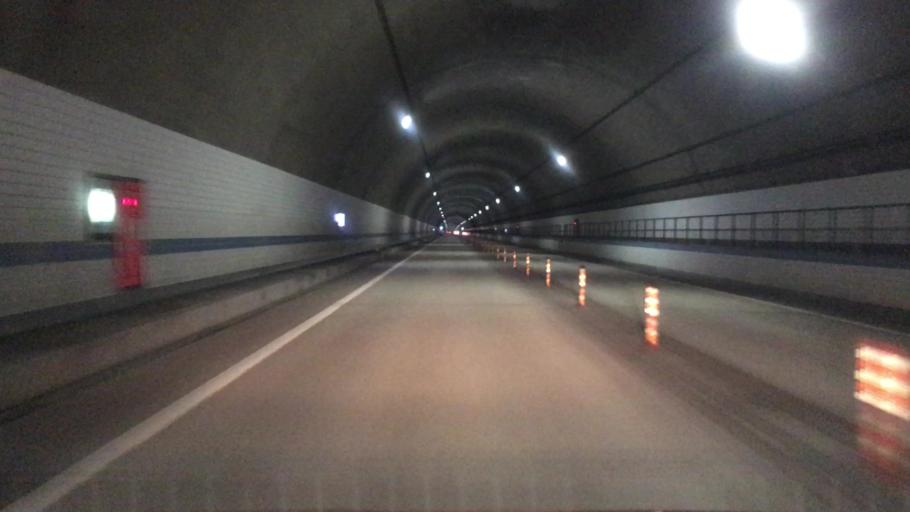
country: JP
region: Hyogo
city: Toyooka
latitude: 35.6297
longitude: 134.5994
